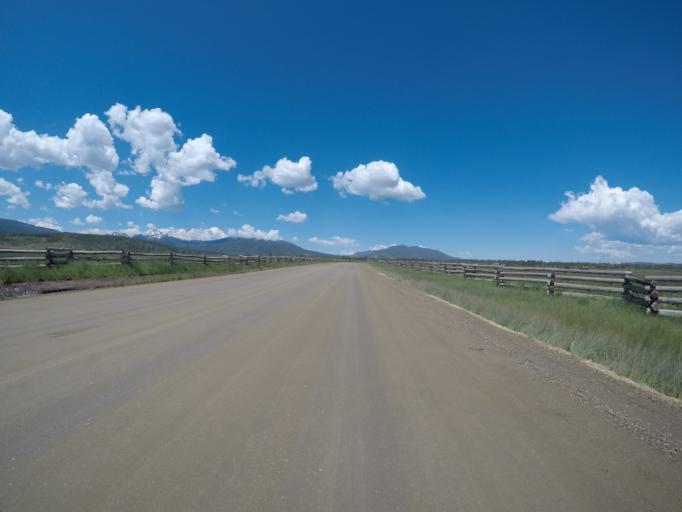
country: US
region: Colorado
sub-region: Grand County
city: Fraser
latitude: 39.9401
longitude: -105.8190
